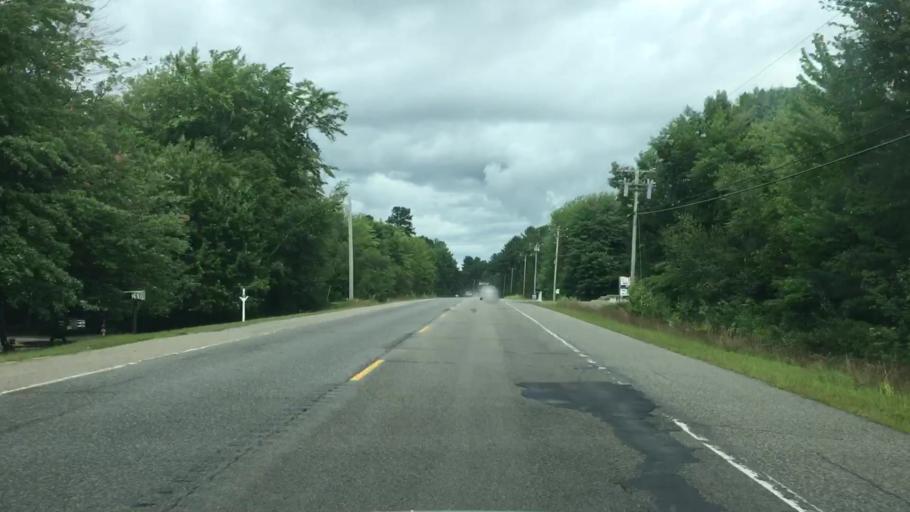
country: US
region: Maine
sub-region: York County
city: South Sanford
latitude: 43.3940
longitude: -70.7393
